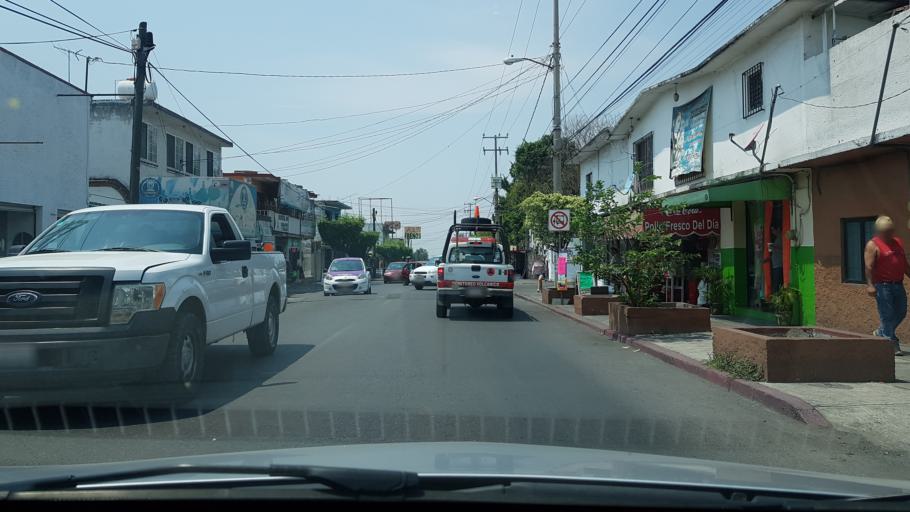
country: MX
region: Morelos
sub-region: Jiutepec
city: Jiutepec
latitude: 18.8941
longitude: -99.1710
